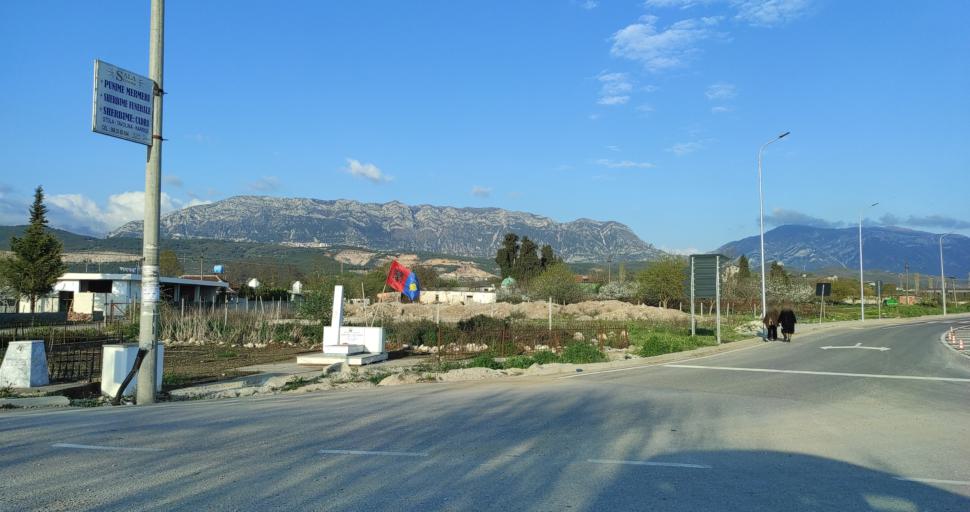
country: AL
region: Durres
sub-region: Rrethi i Krujes
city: Fushe-Kruje
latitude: 41.4869
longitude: 19.7262
